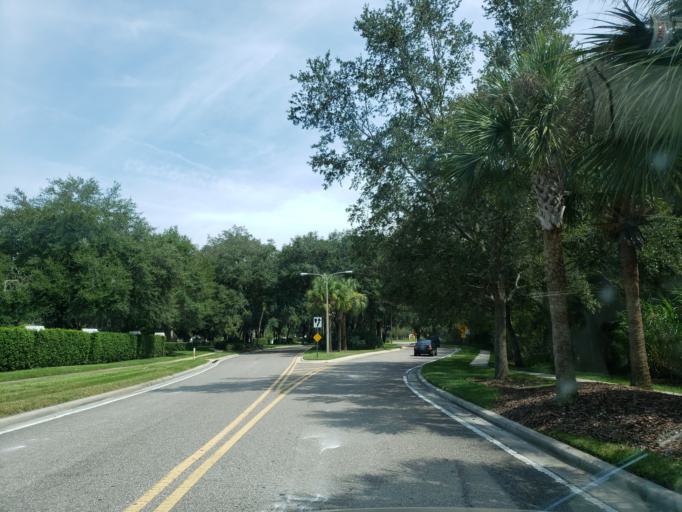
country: US
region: Florida
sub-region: Pasco County
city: Wesley Chapel
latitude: 28.2234
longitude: -82.3860
